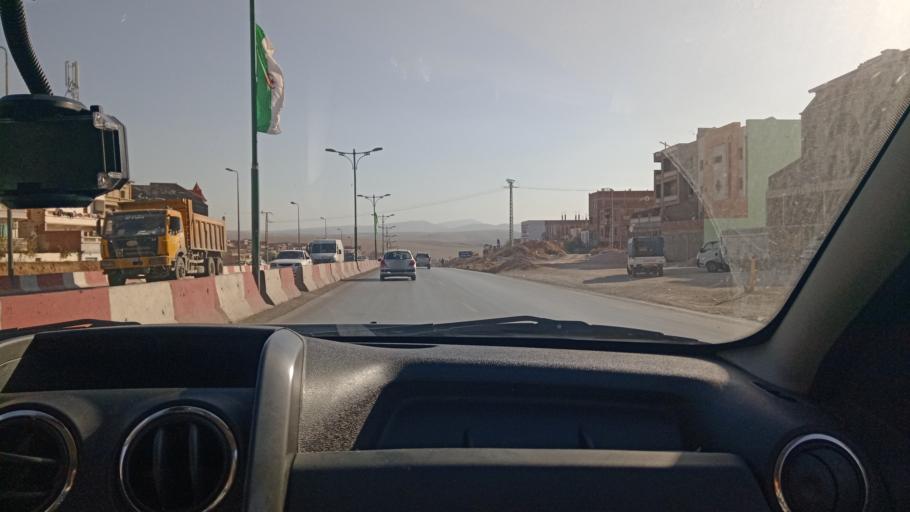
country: DZ
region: Constantine
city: El Khroub
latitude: 36.2571
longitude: 6.7114
